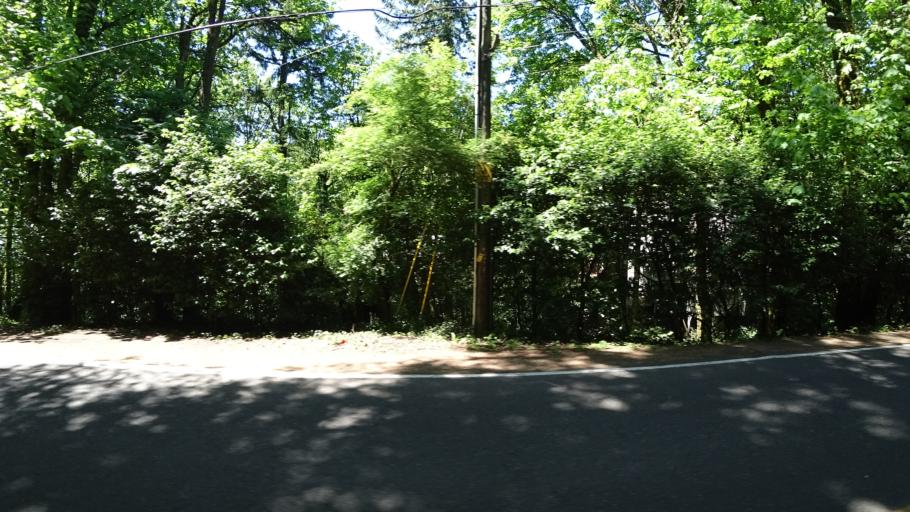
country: US
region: Oregon
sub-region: Multnomah County
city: Portland
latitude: 45.4954
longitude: -122.7061
